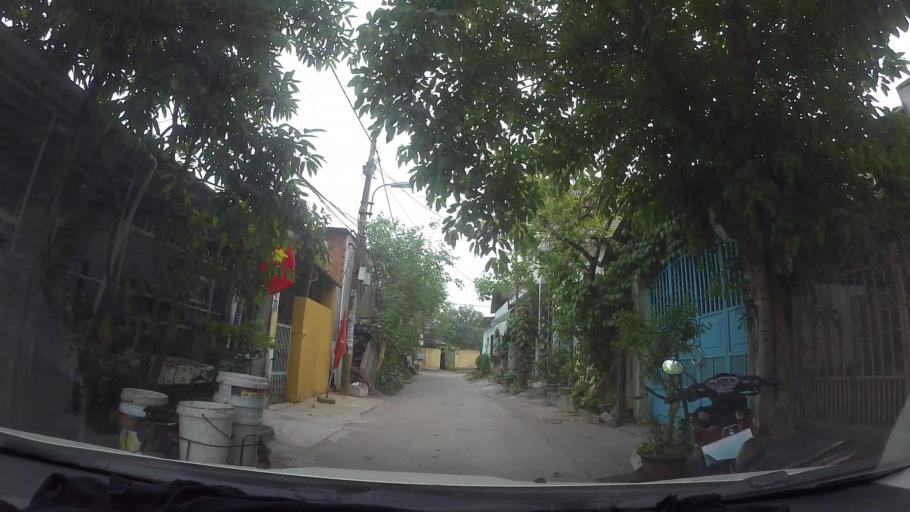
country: VN
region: Da Nang
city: Lien Chieu
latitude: 16.0677
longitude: 108.1426
